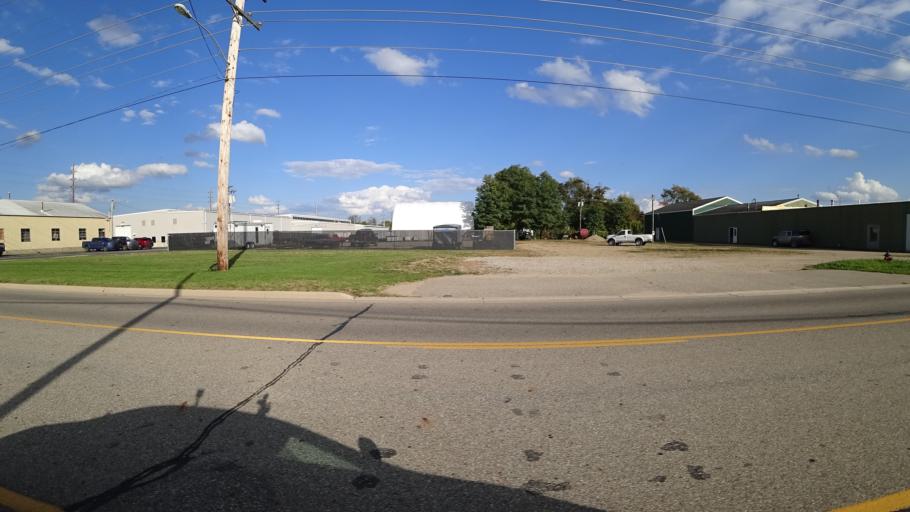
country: US
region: Michigan
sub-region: Saint Joseph County
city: Sturgis
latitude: 41.8068
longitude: -85.4284
